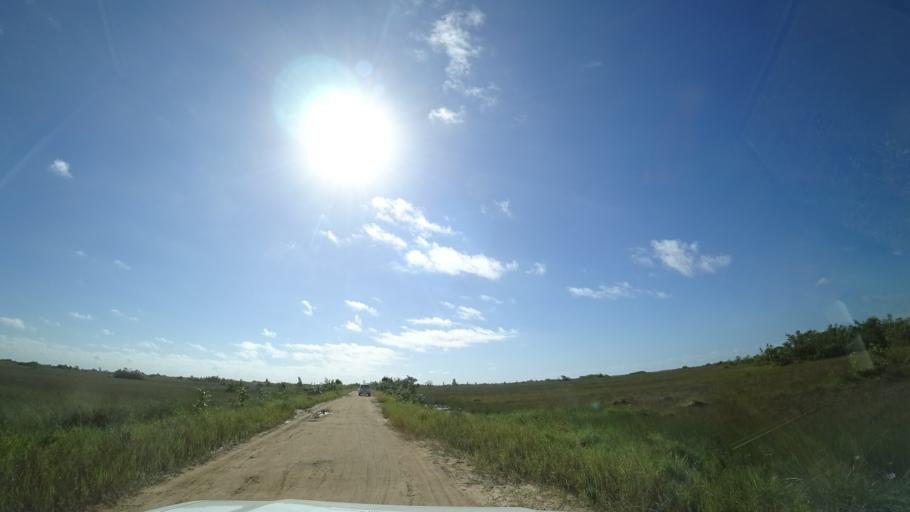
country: MZ
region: Sofala
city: Beira
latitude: -19.6954
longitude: 35.0345
